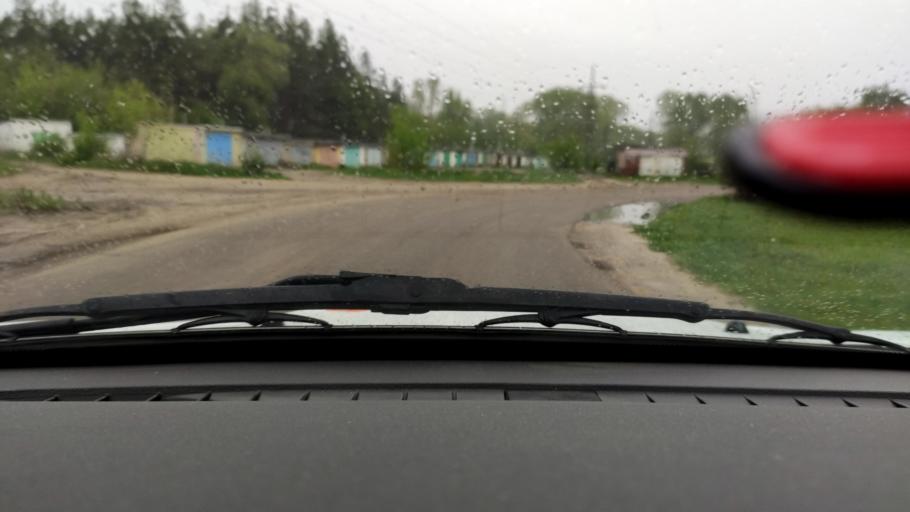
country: RU
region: Voronezj
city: Strelitsa
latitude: 51.6090
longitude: 38.8979
